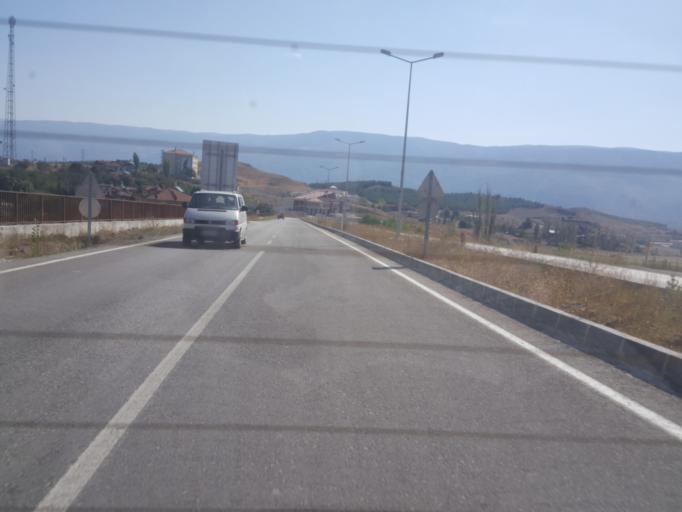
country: TR
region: Kastamonu
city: Tosya
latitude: 41.0070
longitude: 34.0610
